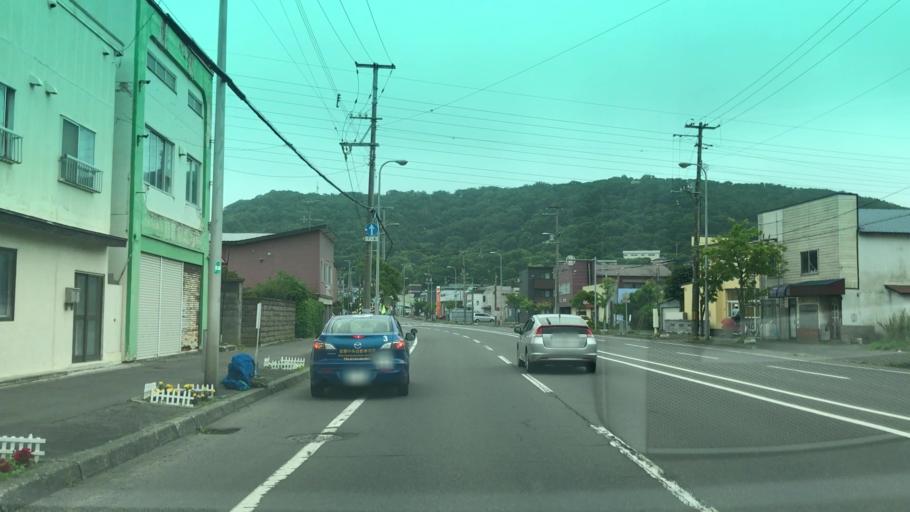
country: JP
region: Hokkaido
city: Muroran
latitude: 42.3571
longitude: 141.0458
